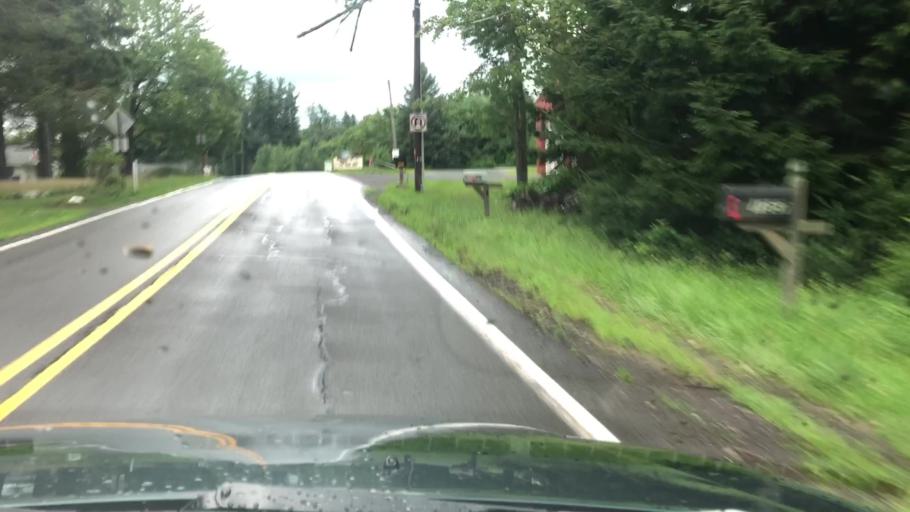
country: US
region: Pennsylvania
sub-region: Monroe County
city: Mountainhome
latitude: 41.3113
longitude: -75.2105
